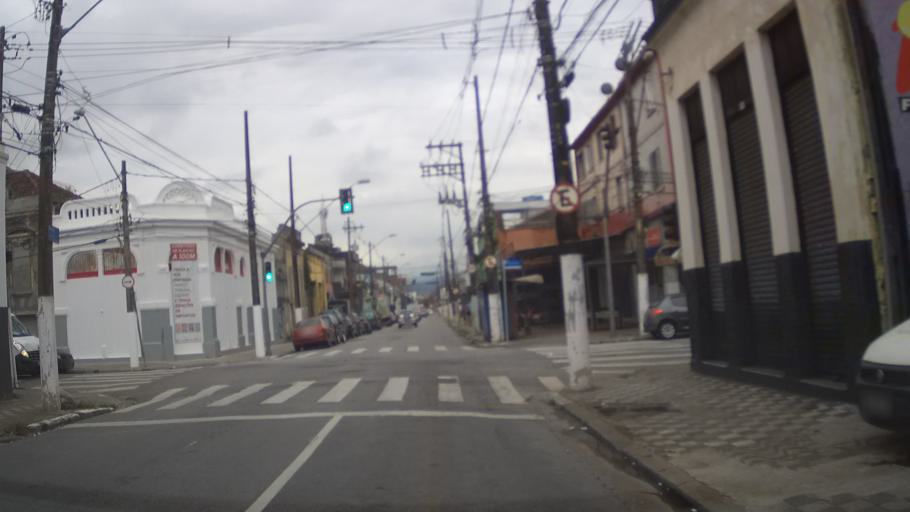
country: BR
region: Sao Paulo
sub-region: Santos
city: Santos
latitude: -23.9375
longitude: -46.3209
